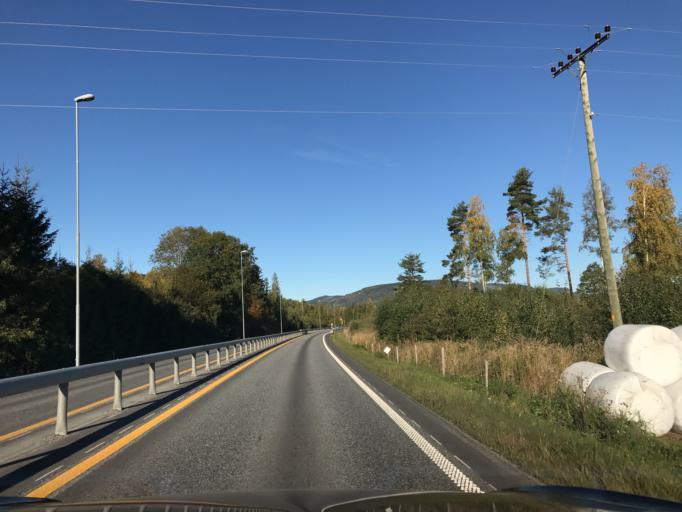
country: NO
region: Oppland
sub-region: Lillehammer
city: Lillehammer
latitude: 61.0184
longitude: 10.4591
